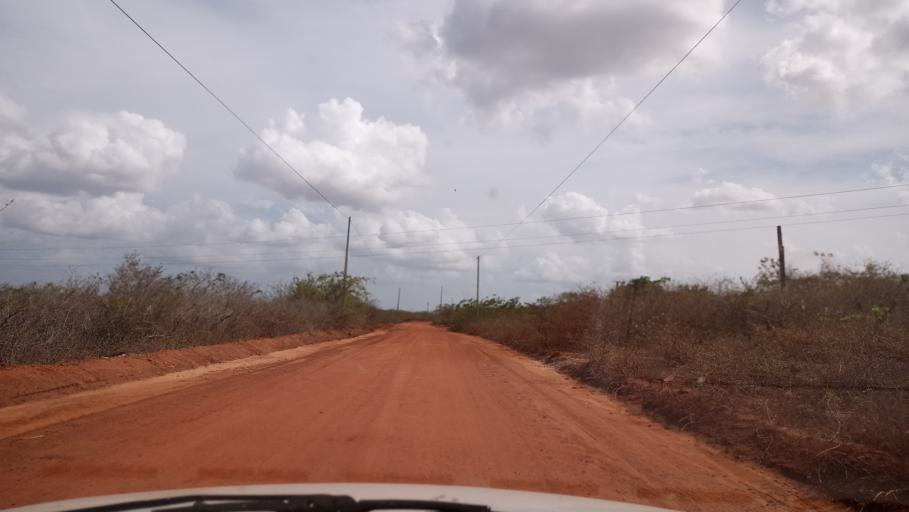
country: BR
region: Rio Grande do Norte
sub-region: Joao Camara
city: Joao Camara
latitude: -5.4750
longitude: -35.8275
